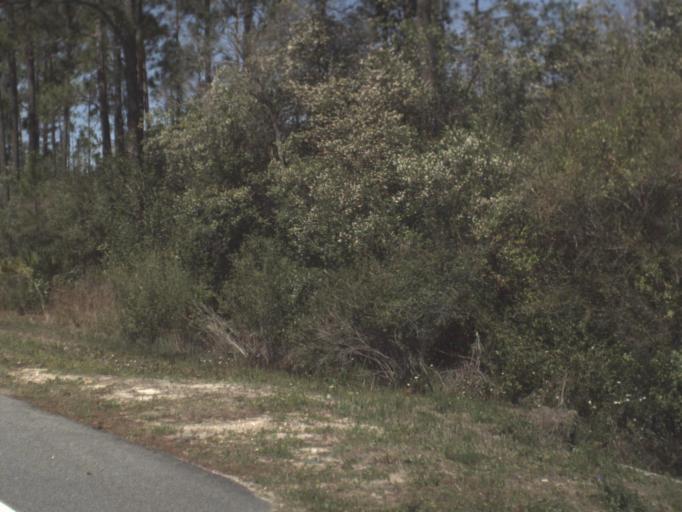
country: US
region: Florida
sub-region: Bay County
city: Lynn Haven
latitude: 30.3221
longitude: -85.6731
